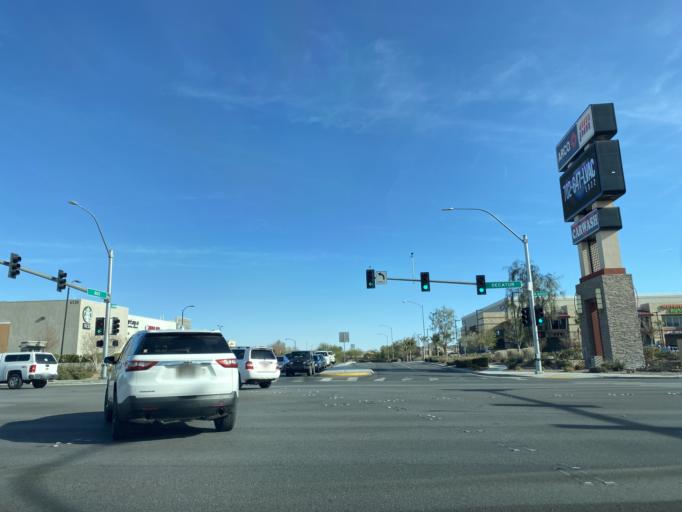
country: US
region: Nevada
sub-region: Clark County
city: North Las Vegas
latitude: 36.2709
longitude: -115.2070
